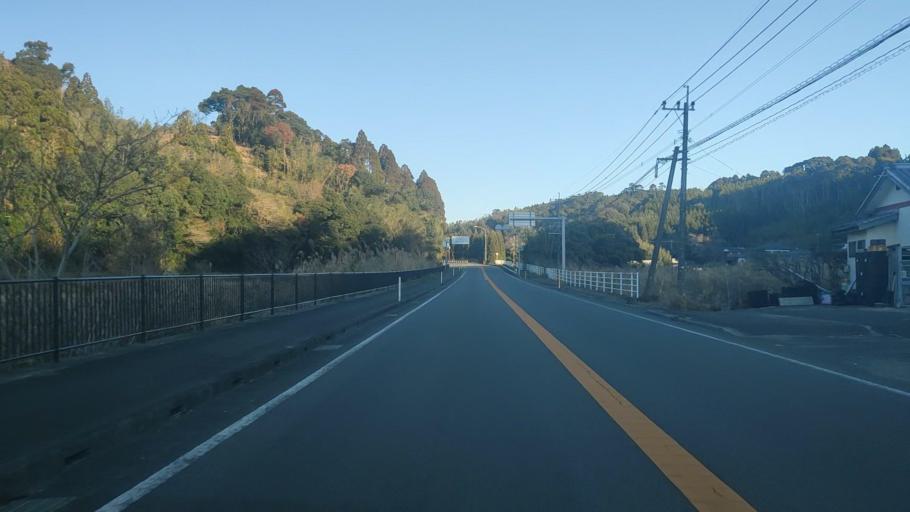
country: JP
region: Miyazaki
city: Takanabe
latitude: 32.1484
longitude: 131.5252
